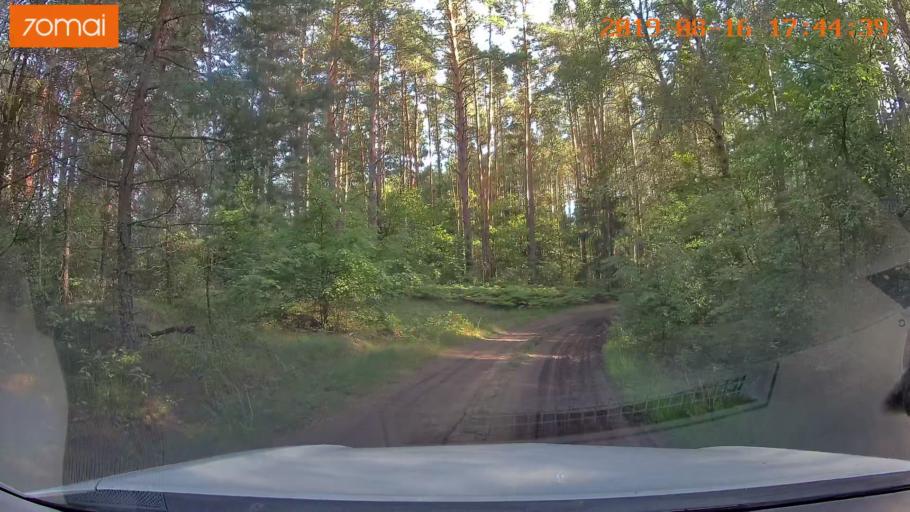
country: BY
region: Mogilev
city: Asipovichy
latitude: 53.2316
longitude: 28.6684
